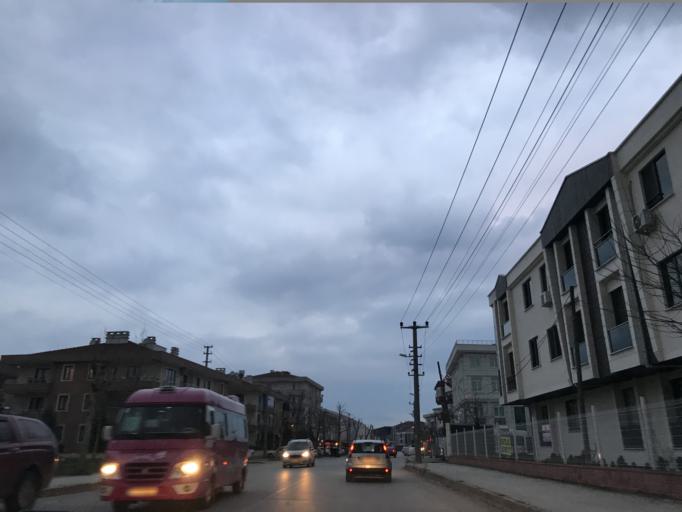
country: TR
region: Yalova
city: Yalova
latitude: 40.6470
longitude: 29.2603
